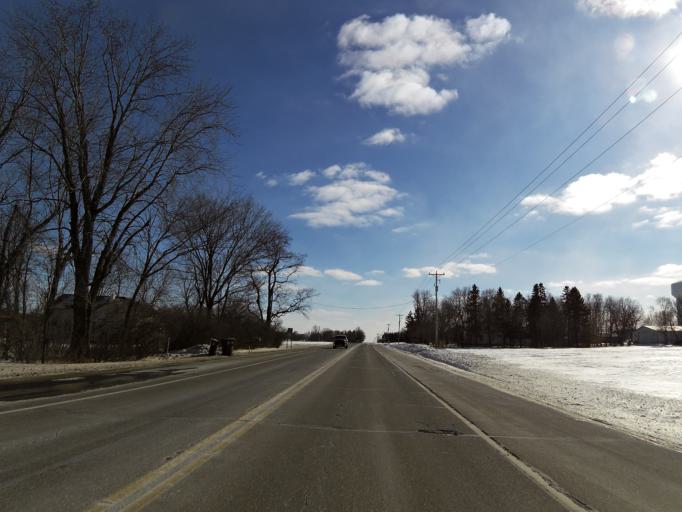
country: US
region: Minnesota
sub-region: Washington County
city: Afton
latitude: 44.9056
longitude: -92.8625
